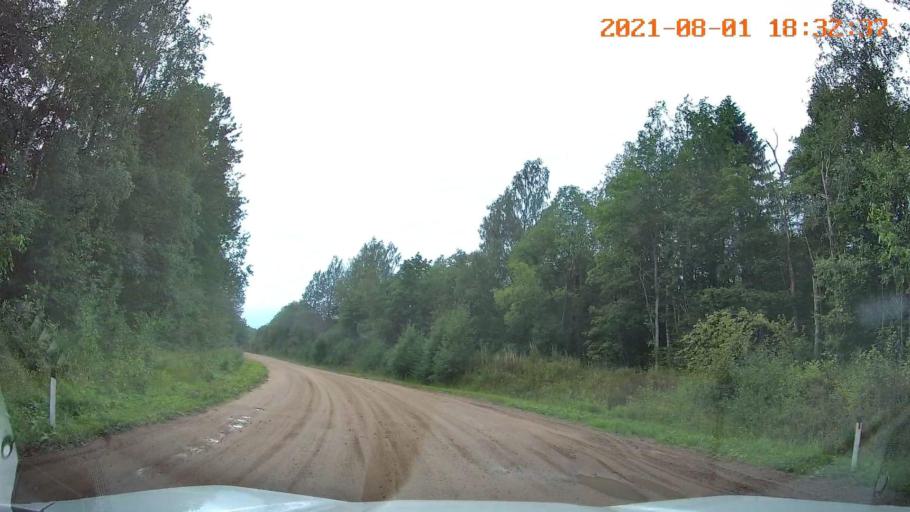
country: RU
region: Leningrad
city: Voznesen'ye
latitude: 60.8922
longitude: 35.3225
